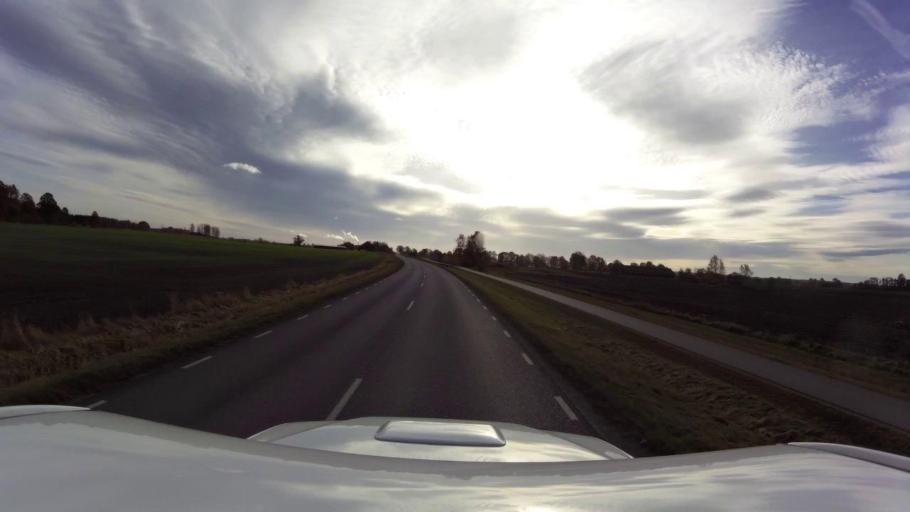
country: SE
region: OEstergoetland
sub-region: Linkopings Kommun
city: Ekangen
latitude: 58.4578
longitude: 15.6403
